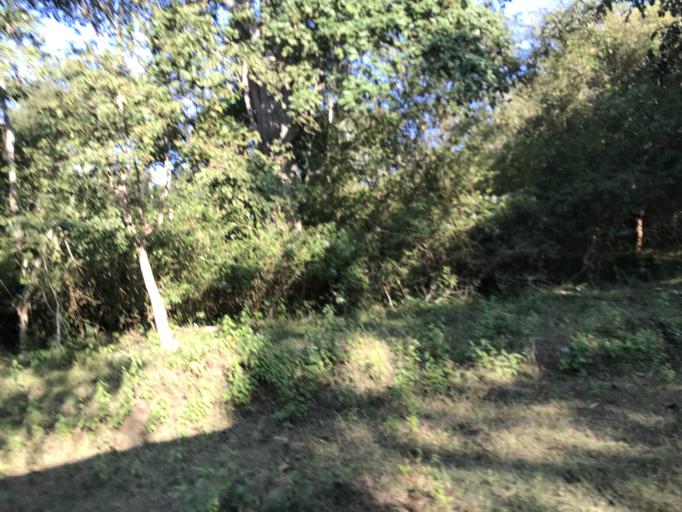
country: IN
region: Karnataka
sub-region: Mysore
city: Heggadadevankote
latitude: 11.9960
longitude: 76.2455
